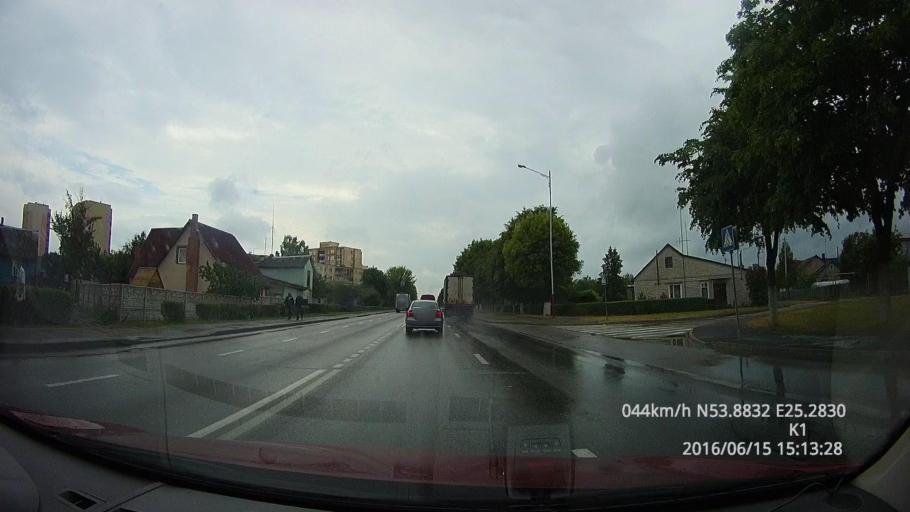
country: BY
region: Grodnenskaya
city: Lida
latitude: 53.8830
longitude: 25.2827
